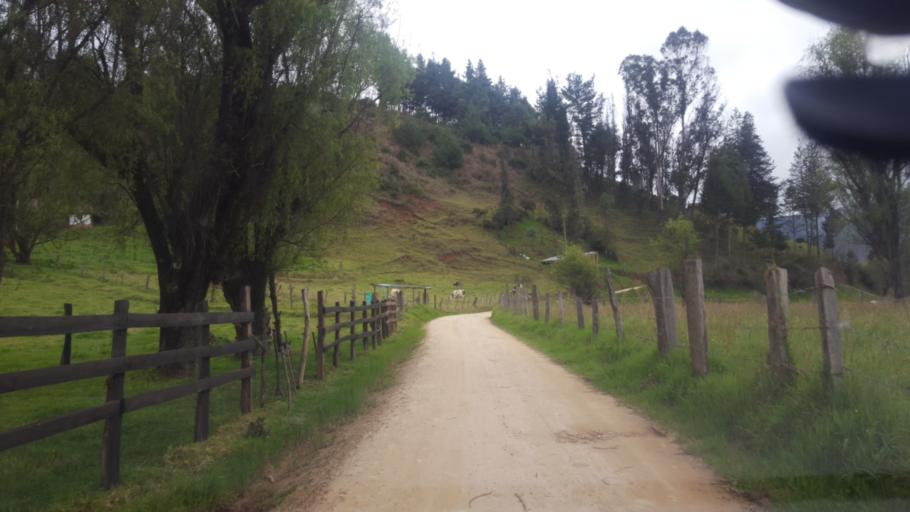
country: CO
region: Boyaca
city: Belen
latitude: 6.0136
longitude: -72.8643
